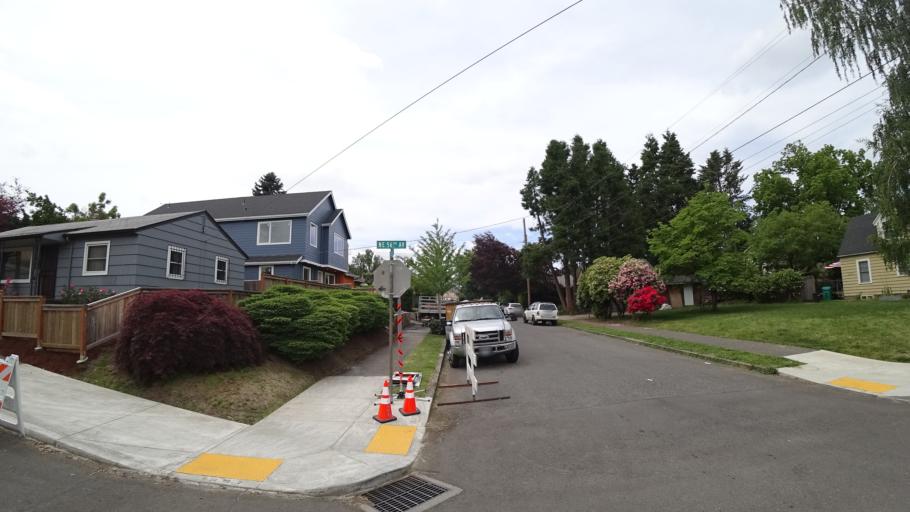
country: US
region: Oregon
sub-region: Multnomah County
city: Lents
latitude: 45.5242
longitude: -122.6064
